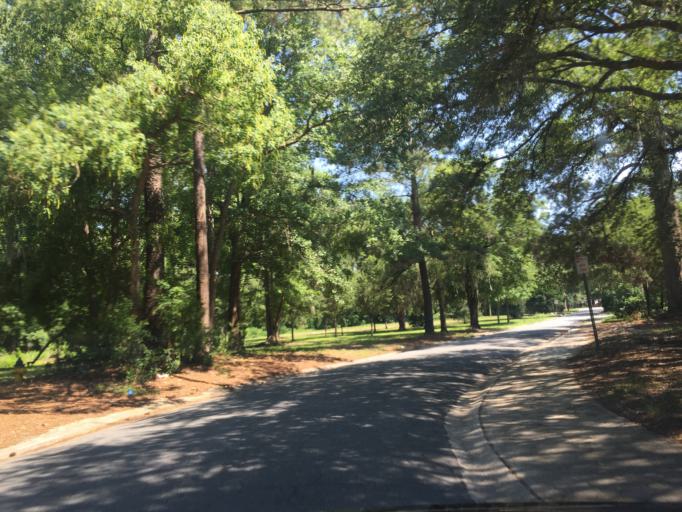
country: US
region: Georgia
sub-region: Chatham County
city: Montgomery
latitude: 31.9757
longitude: -81.1389
